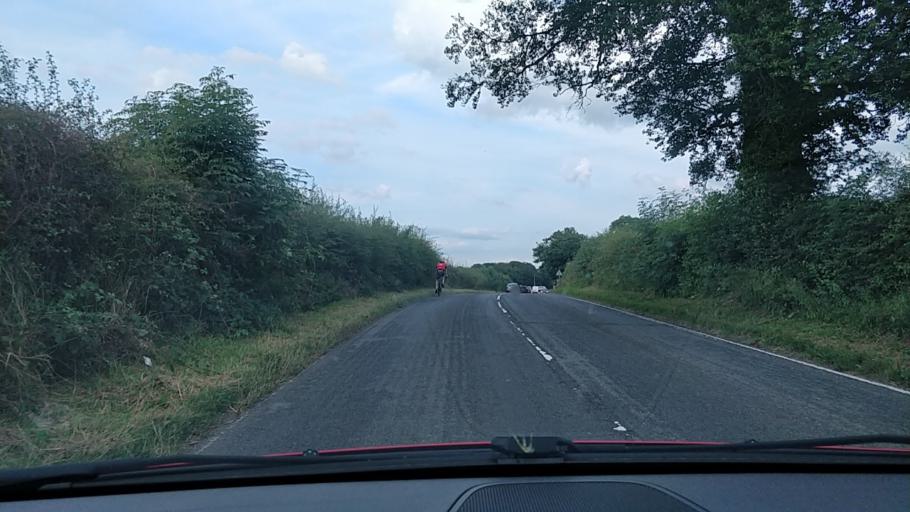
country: GB
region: Wales
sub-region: County of Flintshire
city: Leeswood
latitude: 53.1416
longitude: -3.0807
